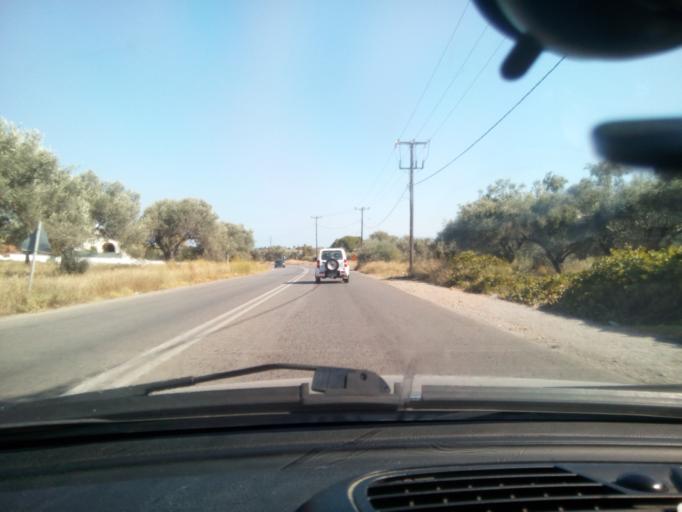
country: GR
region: Central Greece
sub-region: Nomos Evvoias
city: Malakonta
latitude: 38.4061
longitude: 23.7423
